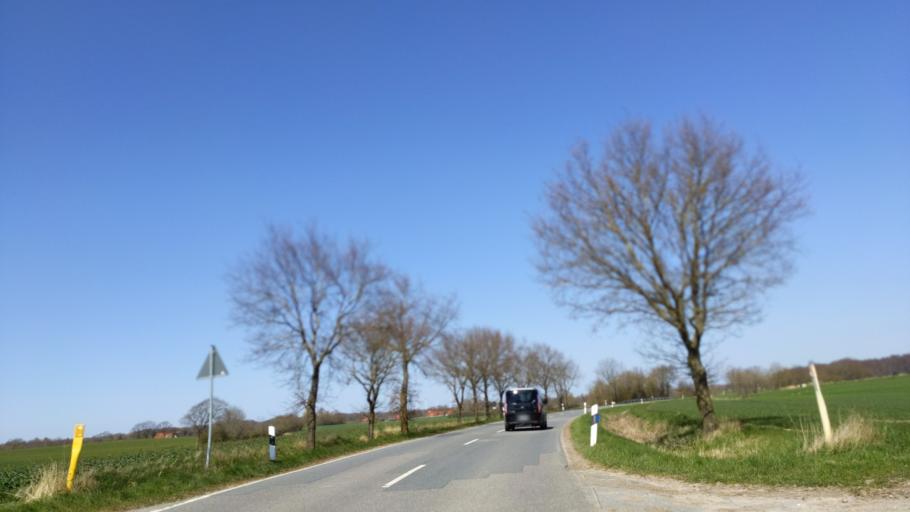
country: DE
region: Schleswig-Holstein
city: Ahrensbok
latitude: 54.0070
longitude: 10.6544
